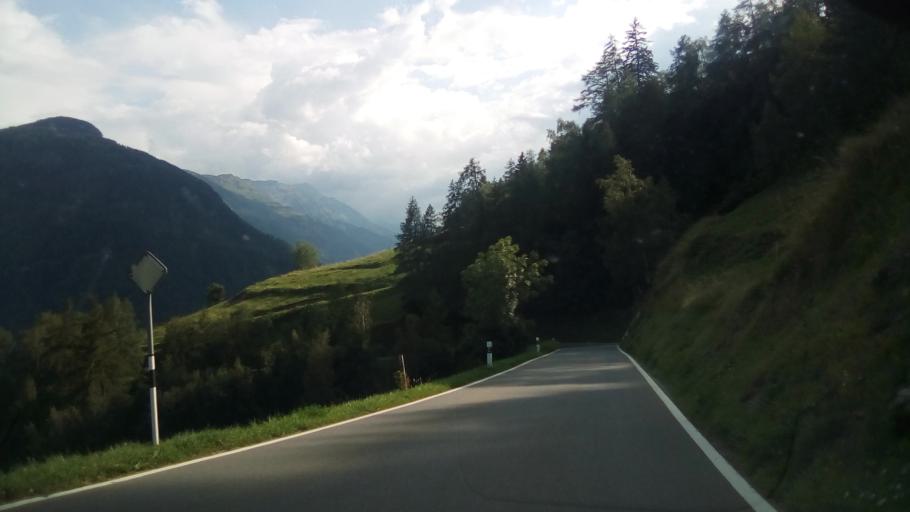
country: CH
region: Valais
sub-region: Entremont District
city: Orsieres
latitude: 46.0328
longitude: 7.1347
